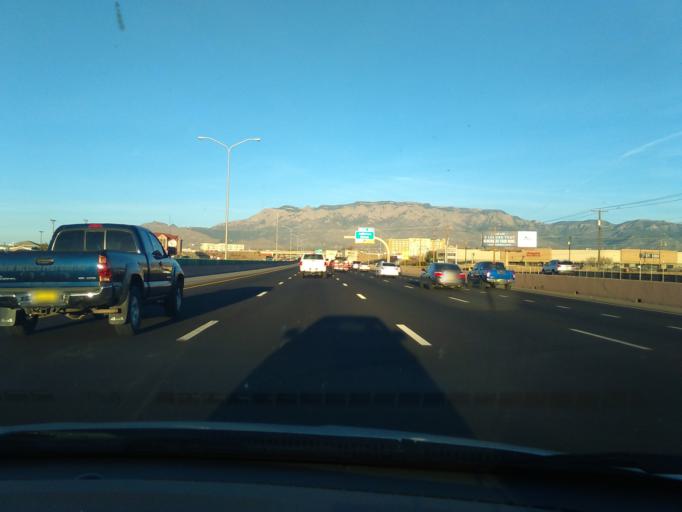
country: US
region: New Mexico
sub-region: Bernalillo County
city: North Valley
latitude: 35.1385
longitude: -106.6001
